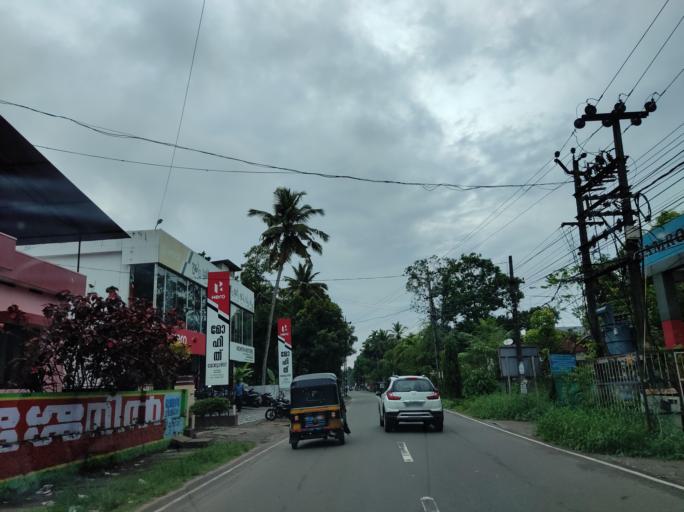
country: IN
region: Kerala
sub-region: Alappuzha
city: Mavelikara
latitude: 9.2515
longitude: 76.5206
